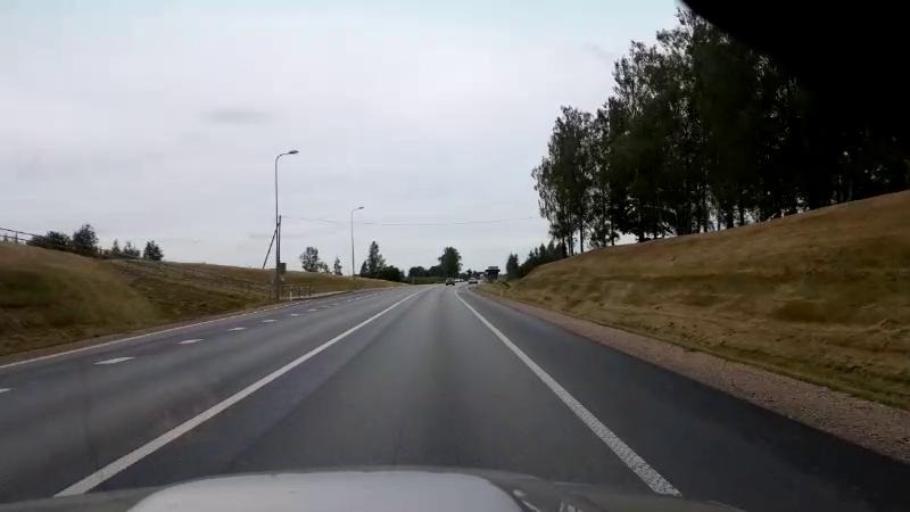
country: LV
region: Lecava
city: Iecava
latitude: 56.6269
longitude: 24.2213
